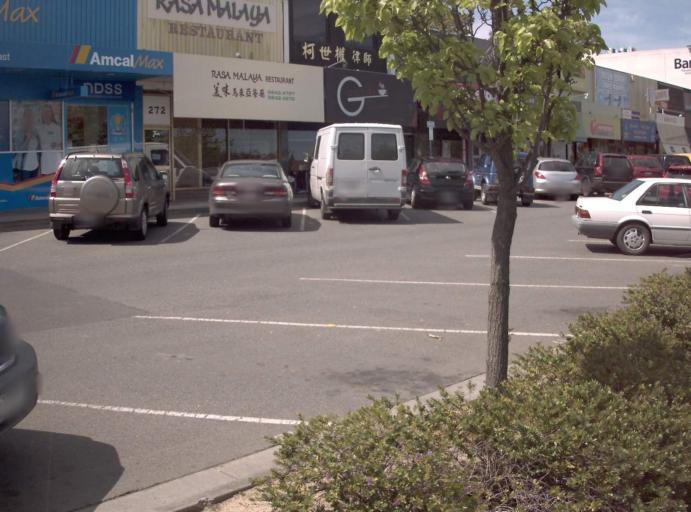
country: AU
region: Victoria
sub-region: Manningham
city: Donvale
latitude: -37.7820
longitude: 145.1634
